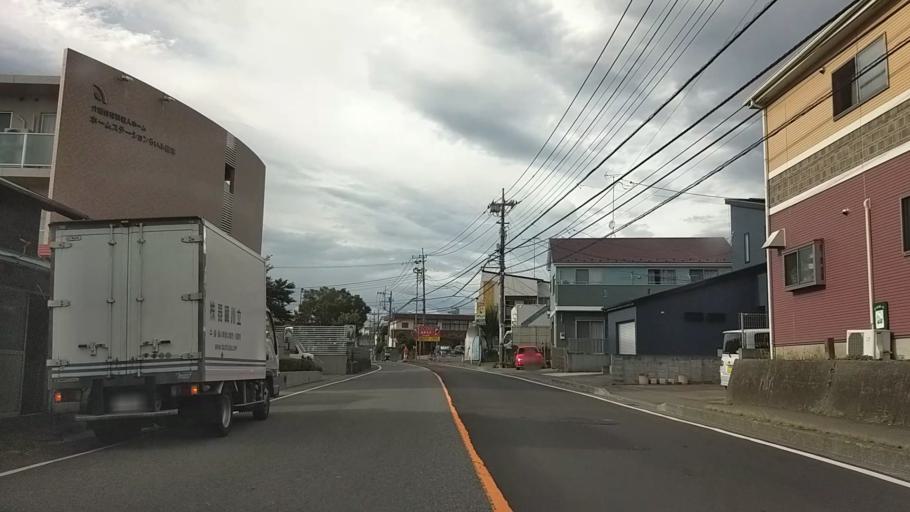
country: JP
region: Tokyo
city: Hachioji
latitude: 35.5719
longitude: 139.3405
